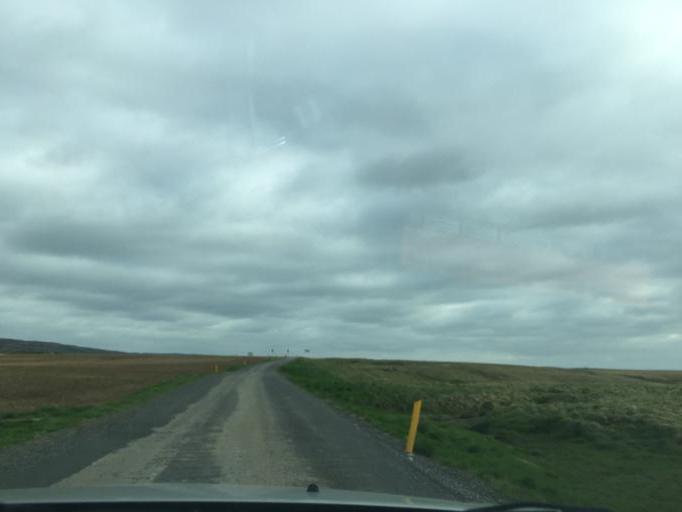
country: IS
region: South
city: Vestmannaeyjar
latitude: 64.2786
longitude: -20.2256
